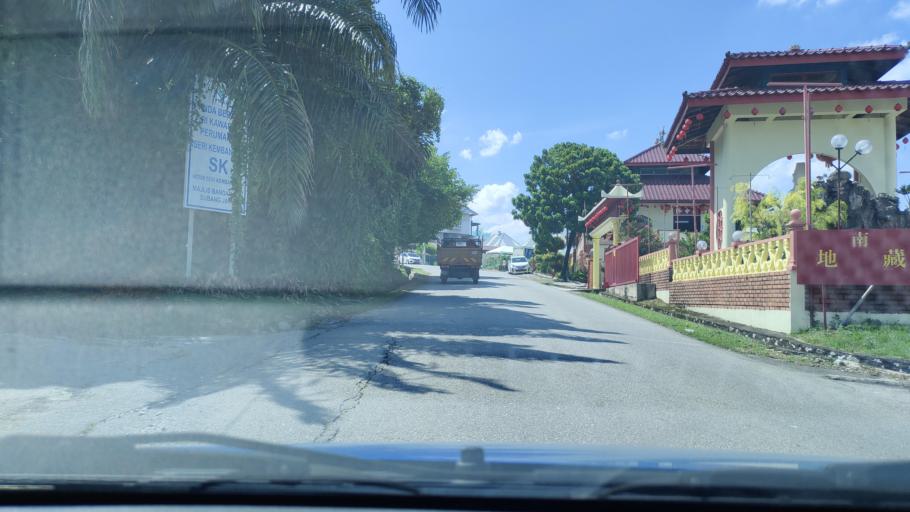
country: MY
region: Selangor
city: Kampong Baharu Balakong
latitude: 3.0287
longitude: 101.7002
